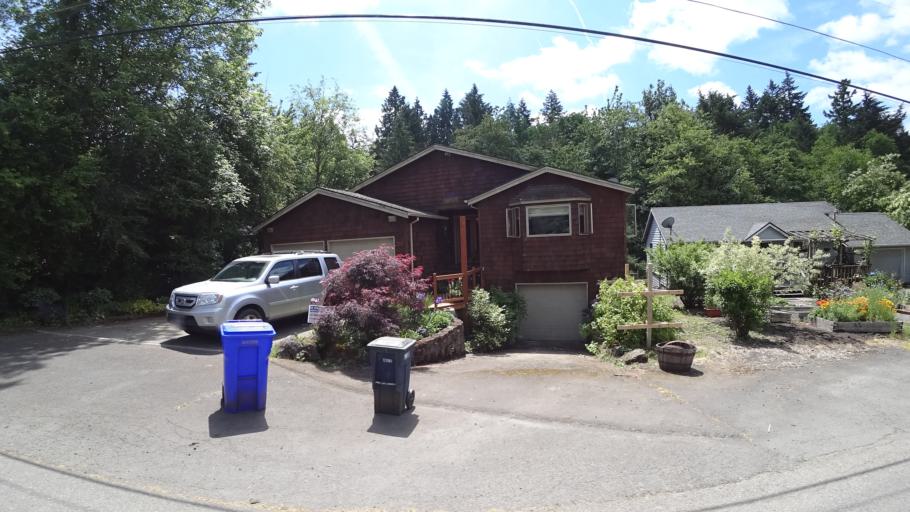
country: US
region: Oregon
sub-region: Washington County
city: Garden Home-Whitford
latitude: 45.4605
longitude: -122.7228
